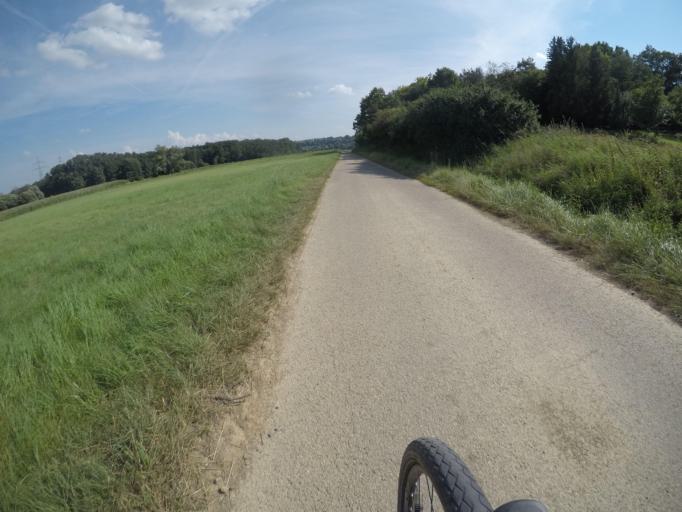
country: DE
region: Baden-Wuerttemberg
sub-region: Karlsruhe Region
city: Olbronn-Durrn
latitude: 48.9705
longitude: 8.7517
